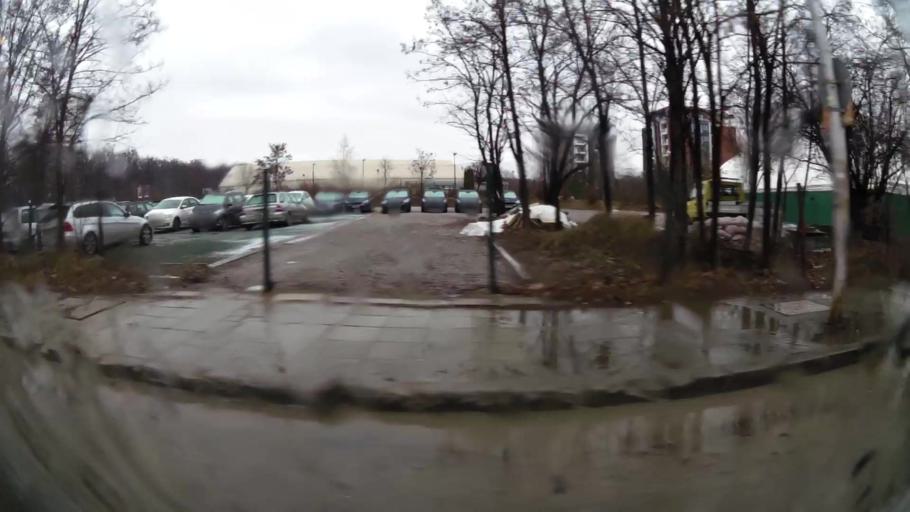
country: BG
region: Sofia-Capital
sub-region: Stolichna Obshtina
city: Sofia
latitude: 42.6669
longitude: 23.3270
